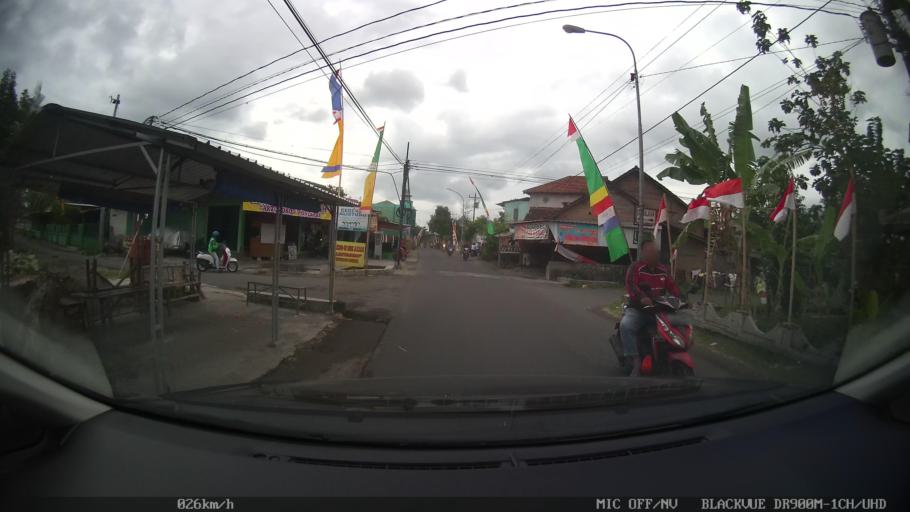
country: ID
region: Daerah Istimewa Yogyakarta
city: Sewon
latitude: -7.8354
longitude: 110.4190
